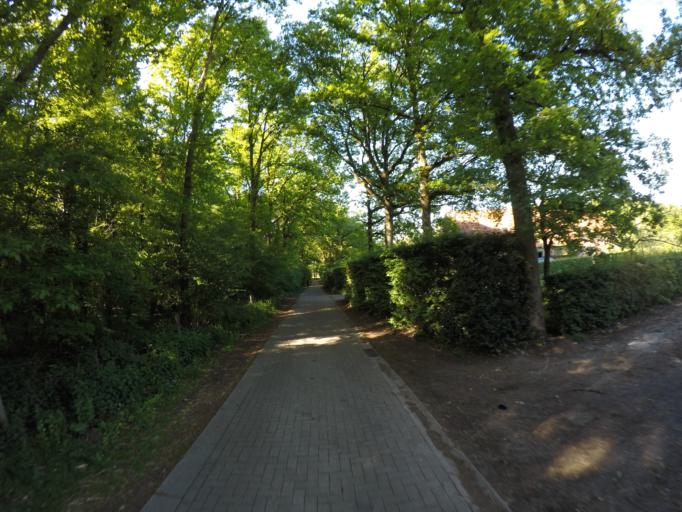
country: BE
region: Flanders
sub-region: Provincie Antwerpen
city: Schilde
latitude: 51.2613
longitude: 4.5643
